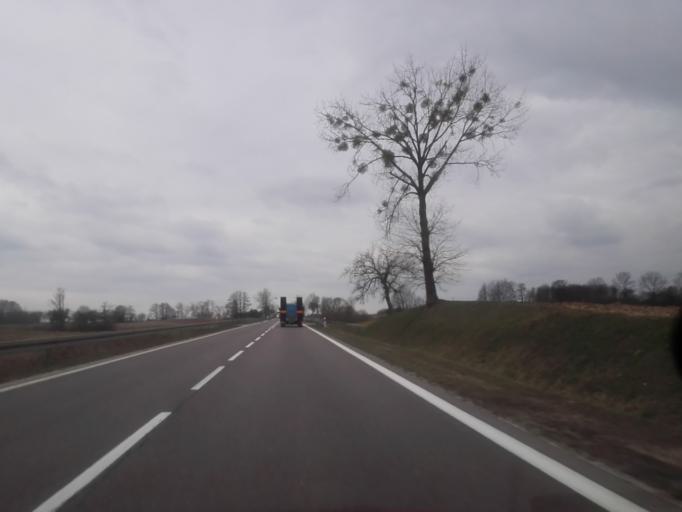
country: PL
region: Podlasie
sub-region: Powiat augustowski
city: Augustow
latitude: 53.8006
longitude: 22.8870
